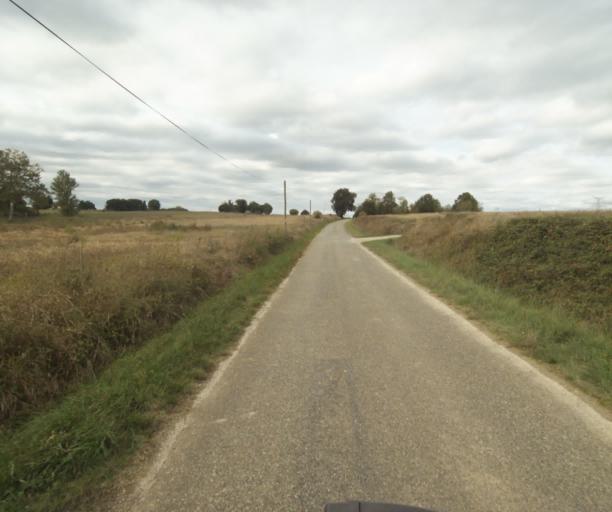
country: FR
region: Midi-Pyrenees
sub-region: Departement du Tarn-et-Garonne
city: Verdun-sur-Garonne
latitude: 43.8660
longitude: 1.1718
